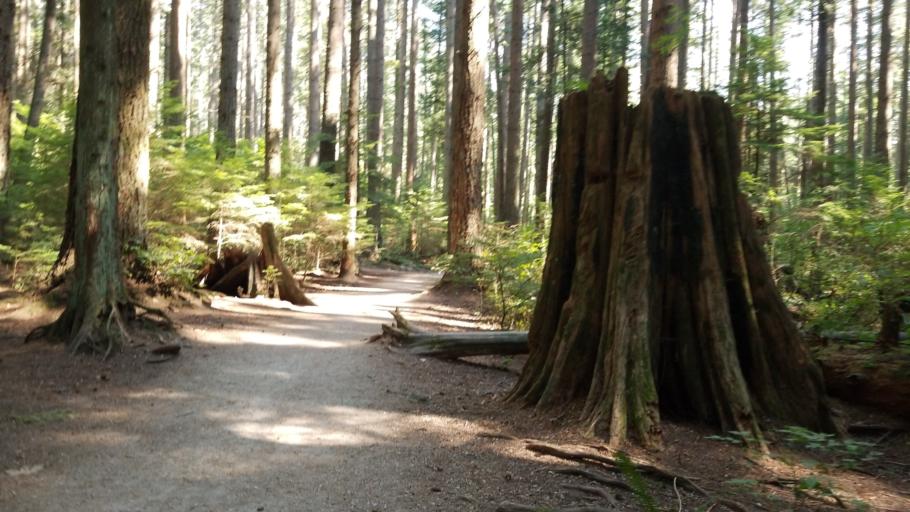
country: CA
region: British Columbia
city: West End
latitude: 49.2517
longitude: -123.2239
